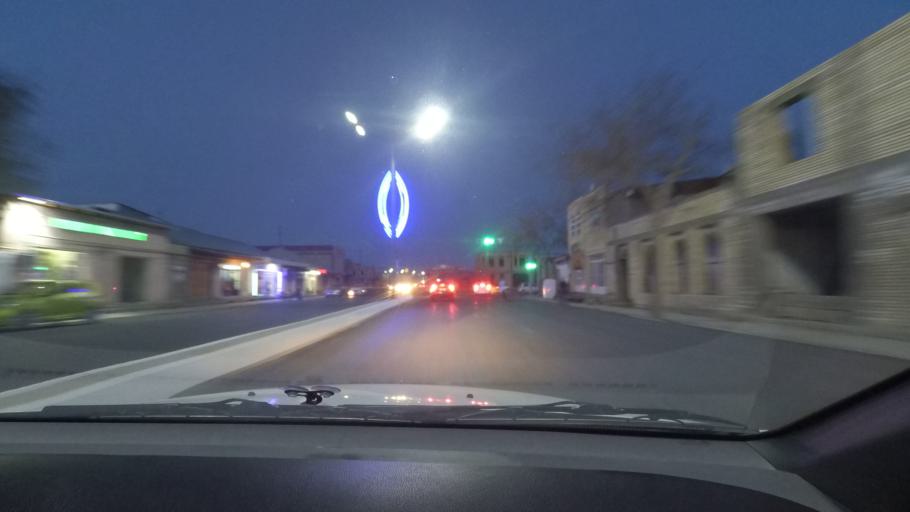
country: UZ
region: Bukhara
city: Bukhara
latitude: 39.7737
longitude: 64.4024
